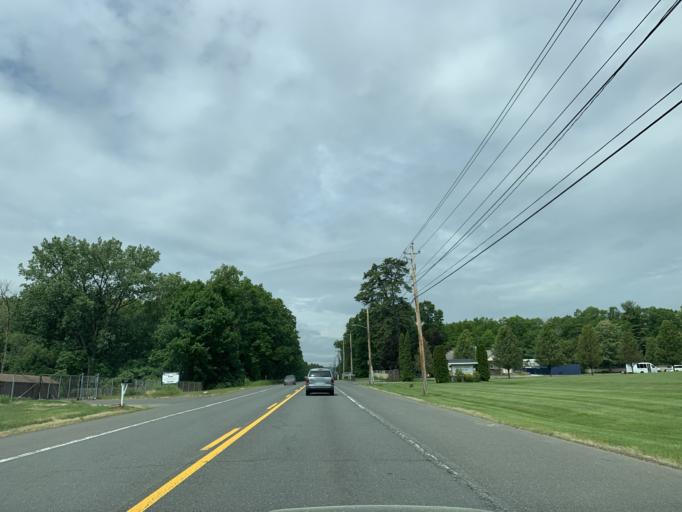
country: US
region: Massachusetts
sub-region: Hampshire County
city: Southampton
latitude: 42.1790
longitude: -72.7038
